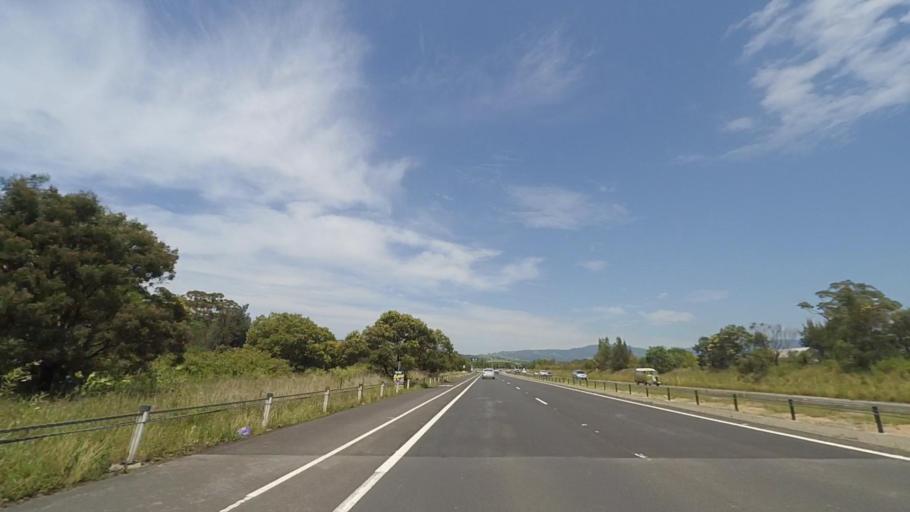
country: AU
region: New South Wales
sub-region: Shellharbour
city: Croom
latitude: -34.6266
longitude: 150.8365
